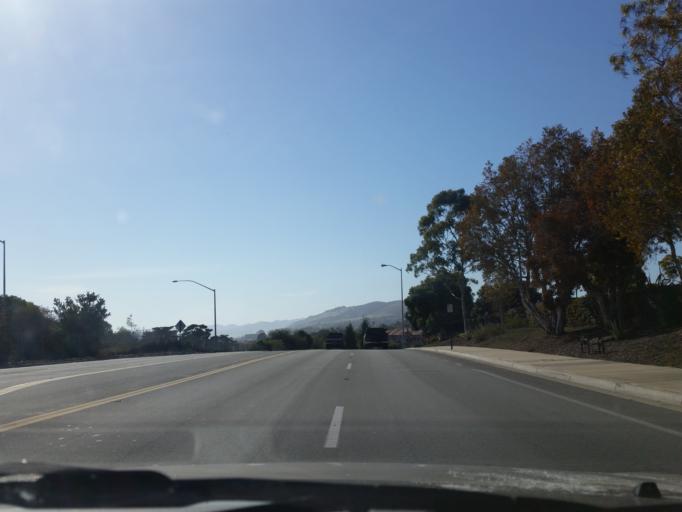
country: US
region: California
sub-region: San Luis Obispo County
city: Arroyo Grande
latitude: 35.1272
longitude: -120.5982
